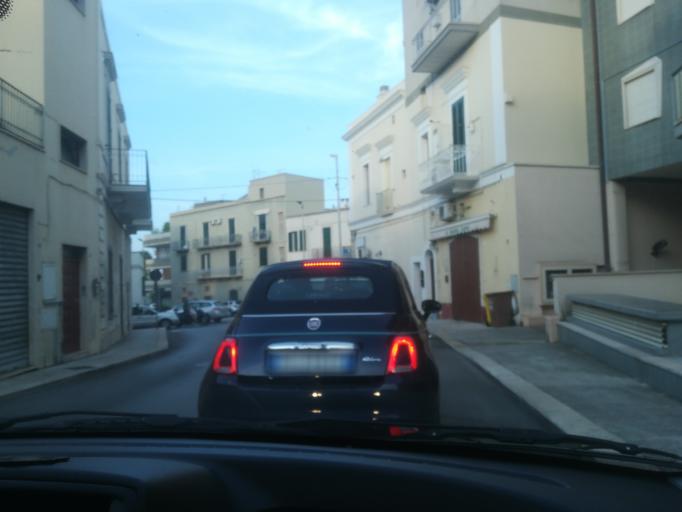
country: IT
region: Apulia
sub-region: Provincia di Bari
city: Monopoli
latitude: 40.9460
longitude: 17.3003
